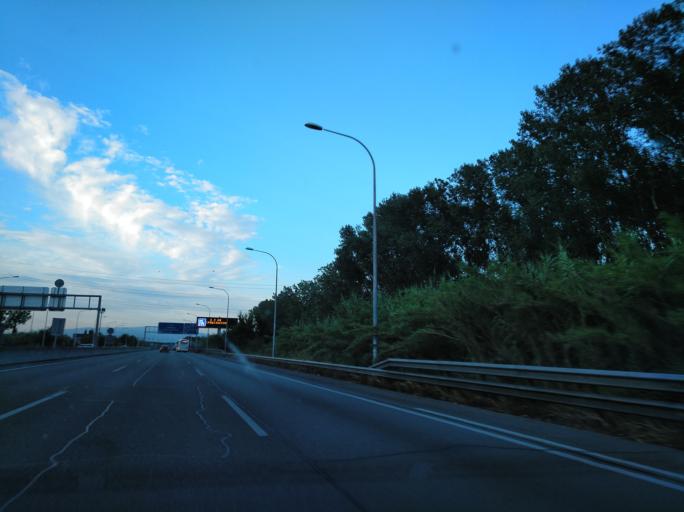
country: ES
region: Catalonia
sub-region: Provincia de Barcelona
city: La Llagosta
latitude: 41.5134
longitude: 2.2069
